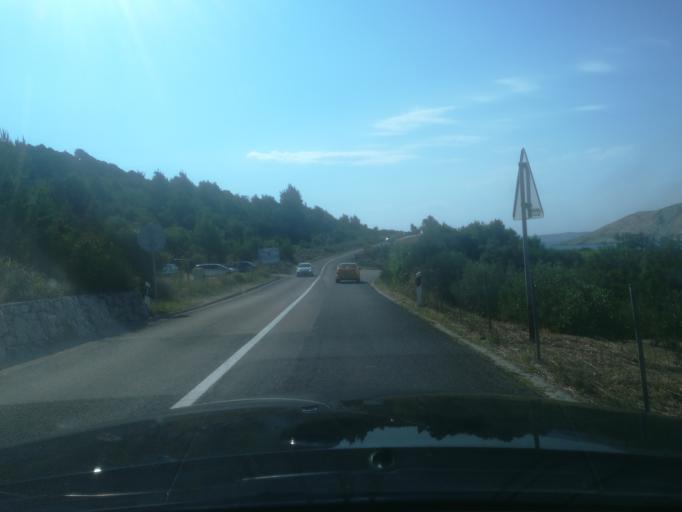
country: HR
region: Primorsko-Goranska
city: Banjol
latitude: 44.7113
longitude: 14.8299
